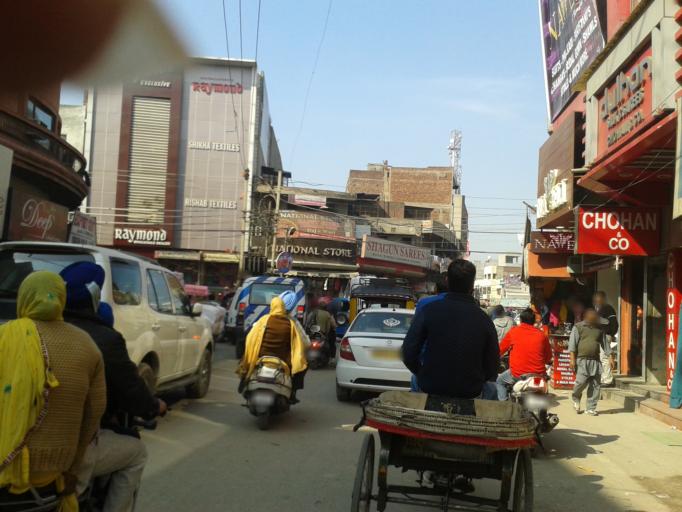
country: IN
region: Punjab
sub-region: Amritsar
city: Amritsar
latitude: 31.6257
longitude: 74.8768
